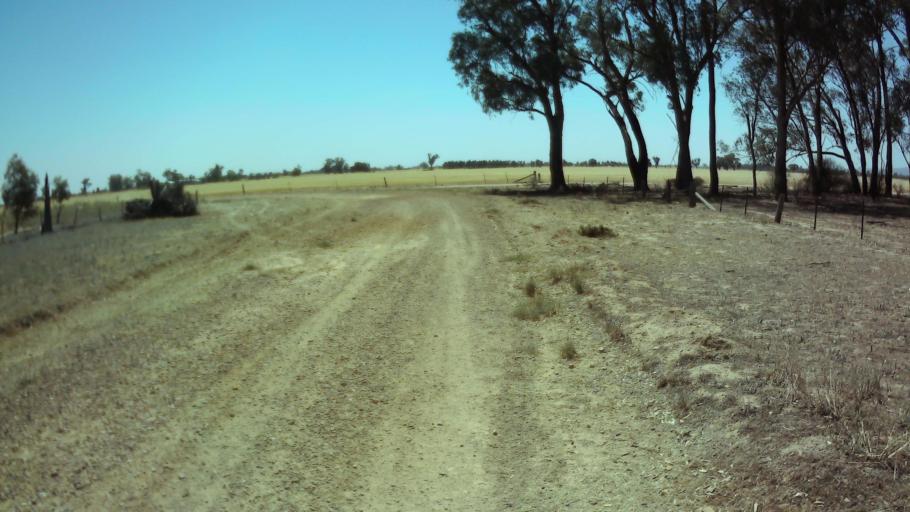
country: AU
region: New South Wales
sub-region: Weddin
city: Grenfell
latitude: -34.0703
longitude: 147.7841
